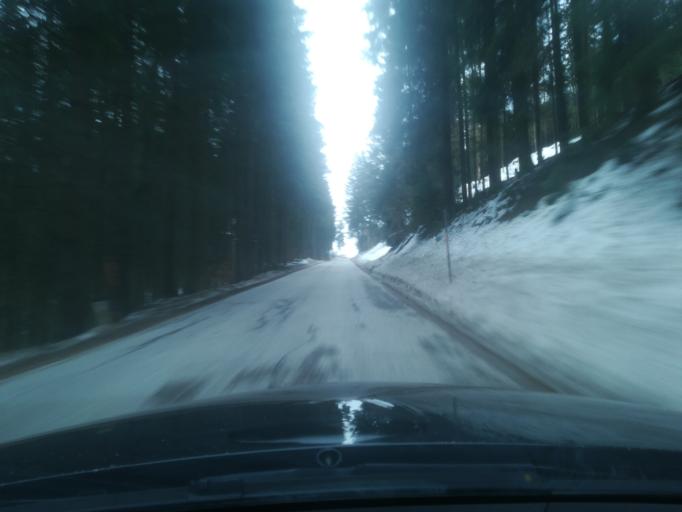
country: AT
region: Upper Austria
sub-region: Politischer Bezirk Perg
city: Perg
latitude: 48.3731
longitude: 14.6315
